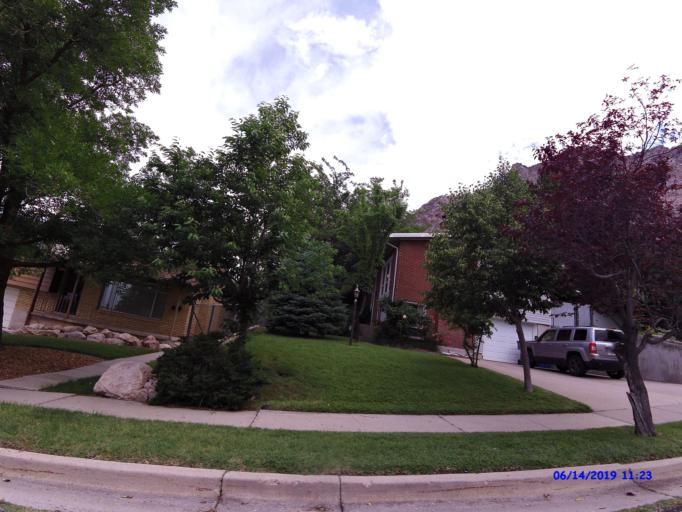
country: US
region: Utah
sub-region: Weber County
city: Ogden
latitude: 41.2584
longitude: -111.9407
